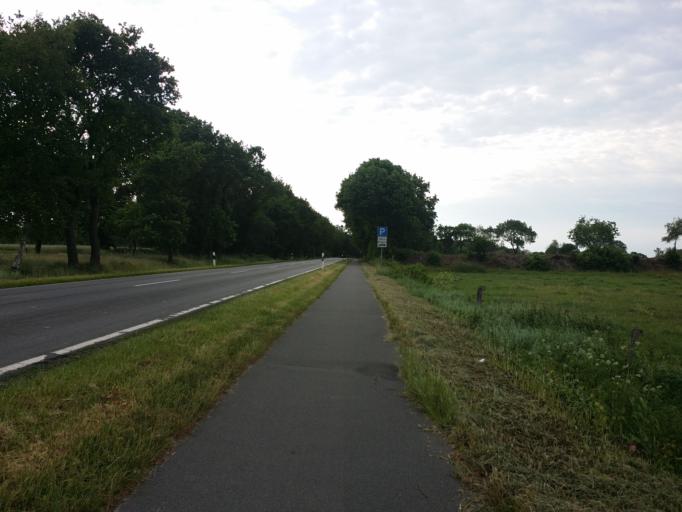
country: DE
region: Lower Saxony
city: Friedeburg
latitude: 53.5104
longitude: 7.7998
